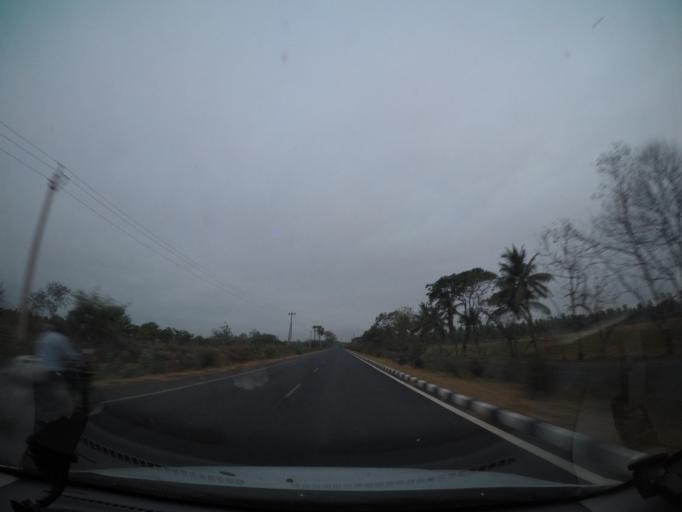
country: IN
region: Andhra Pradesh
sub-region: West Godavari
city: Tadepallegudem
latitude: 16.8066
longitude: 81.3110
